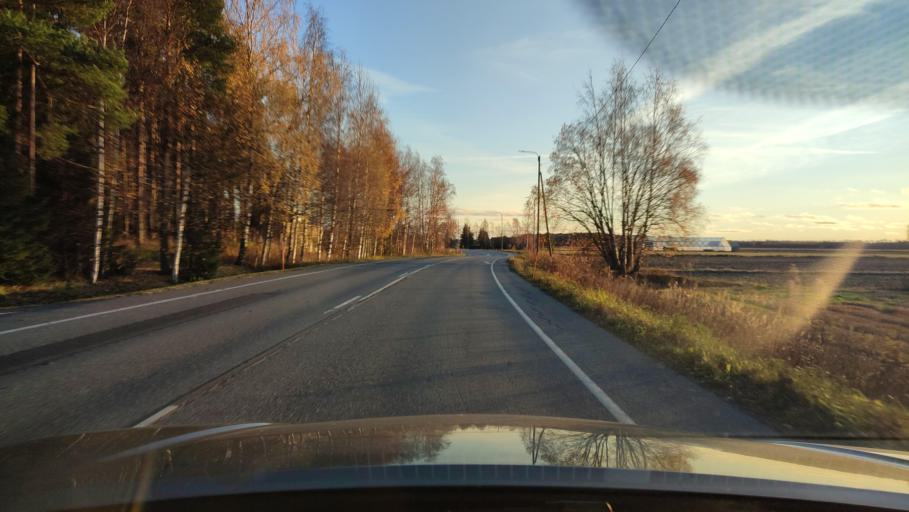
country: FI
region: Ostrobothnia
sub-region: Sydosterbotten
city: Naerpes
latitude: 62.4452
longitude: 21.3513
